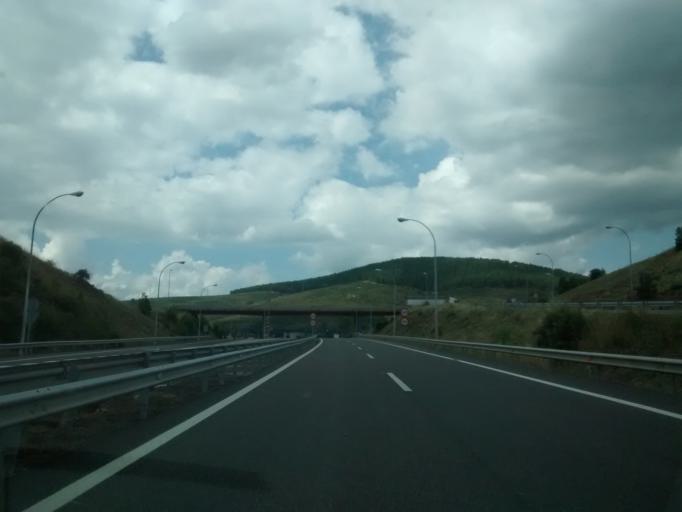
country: ES
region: Castille and Leon
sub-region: Provincia de Leon
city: Carrocera
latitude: 42.7806
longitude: -5.7848
